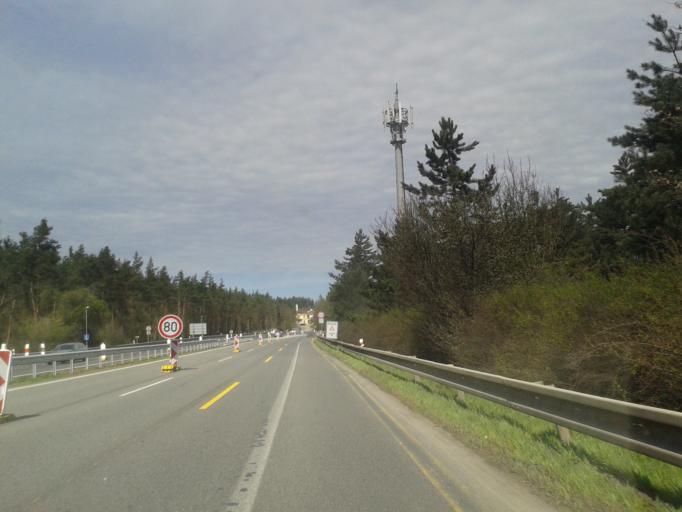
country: CZ
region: Central Bohemia
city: Vsenory
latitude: 49.9199
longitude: 14.3367
